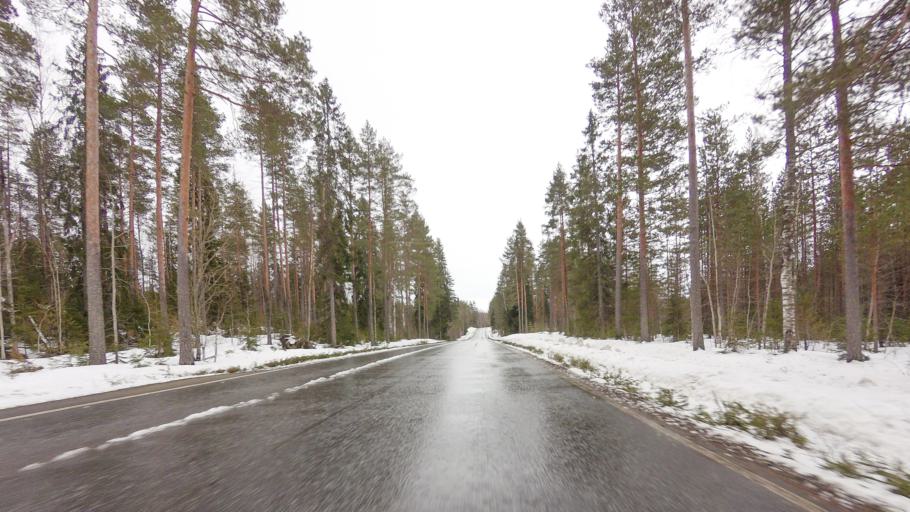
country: FI
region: Southern Savonia
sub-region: Savonlinna
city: Savonlinna
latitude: 61.9777
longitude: 28.8141
